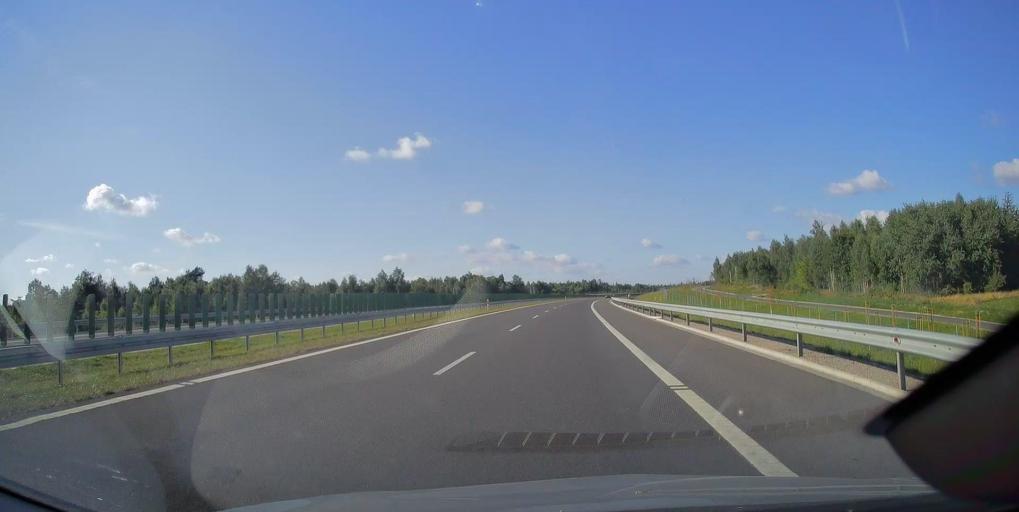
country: PL
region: Swietokrzyskie
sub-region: Powiat skarzyski
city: Skarzysko-Kamienna
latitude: 51.1362
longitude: 20.8329
